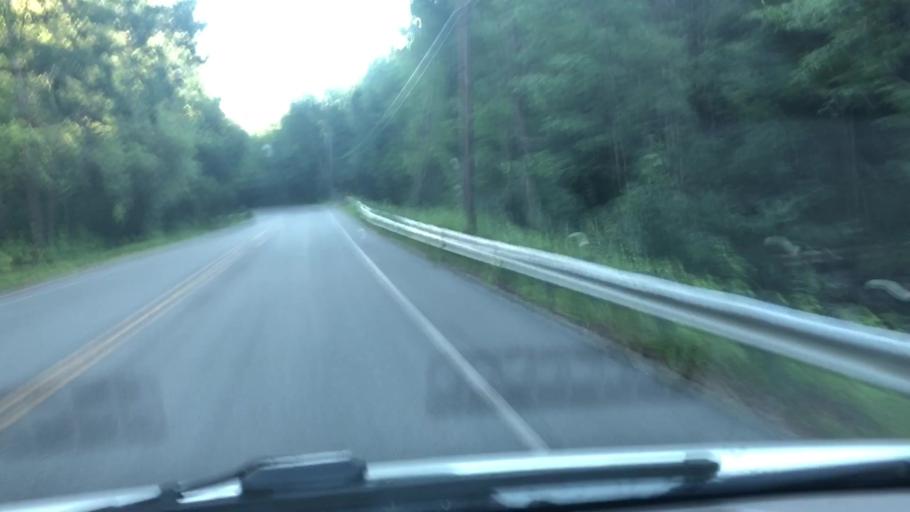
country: US
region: Massachusetts
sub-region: Berkshire County
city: Hinsdale
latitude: 42.4755
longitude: -72.9884
